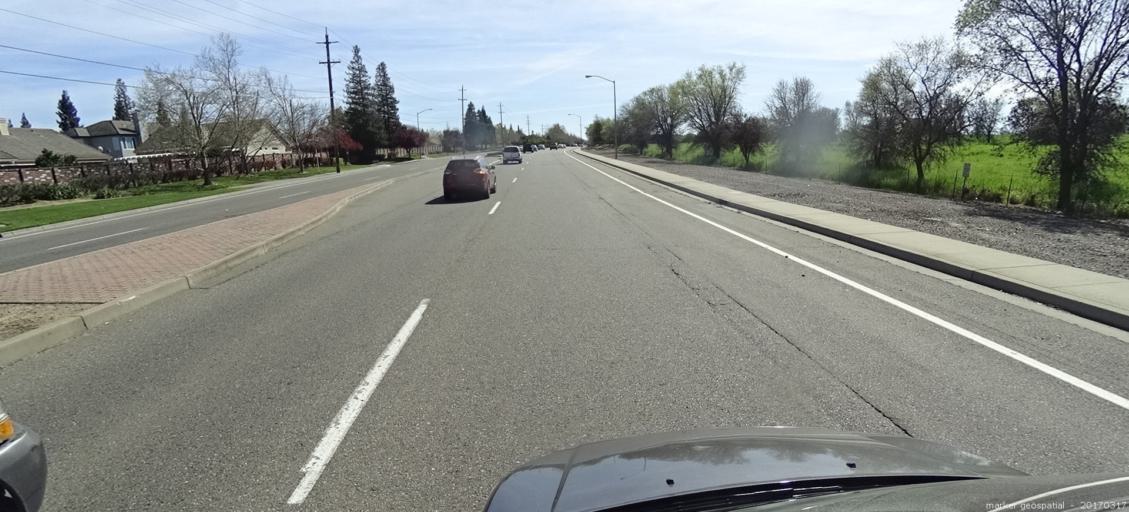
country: US
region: California
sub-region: Sacramento County
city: Laguna
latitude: 38.4459
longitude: -121.4446
